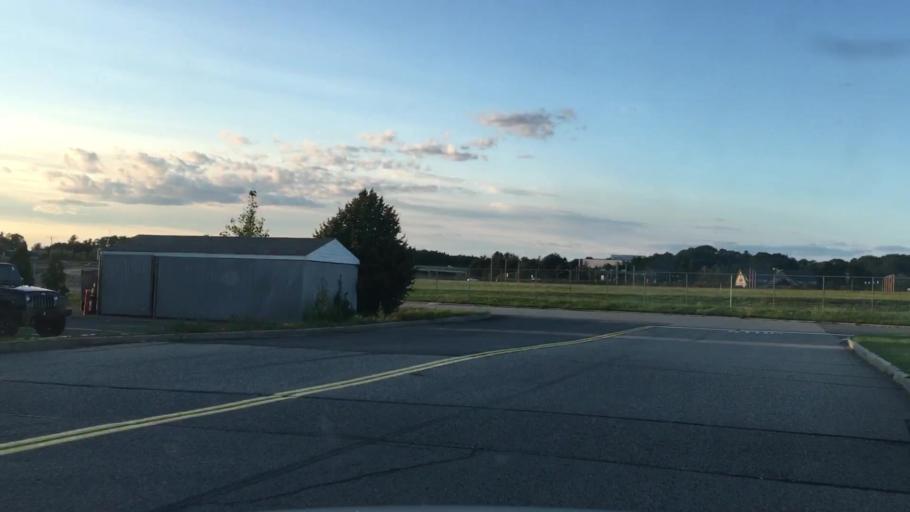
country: US
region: Maine
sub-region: Cumberland County
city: South Portland Gardens
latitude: 43.6439
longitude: -70.3285
